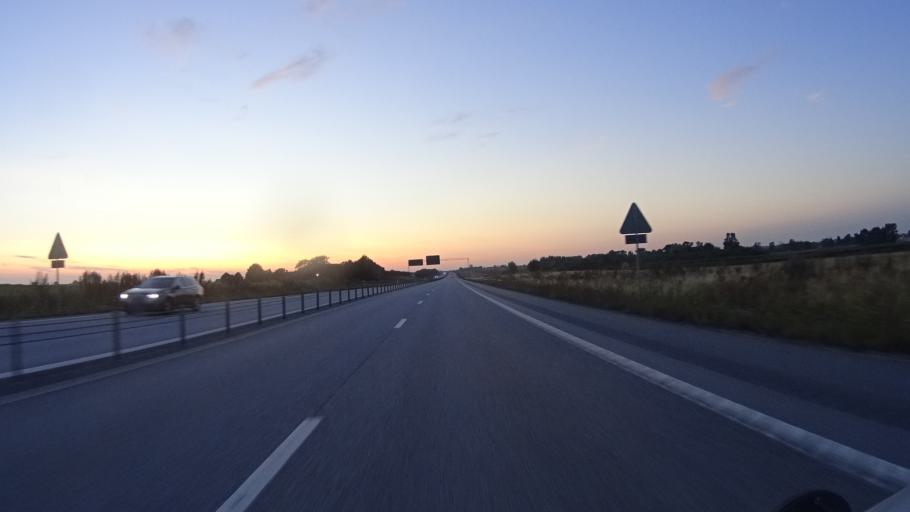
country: SE
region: Skane
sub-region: Trelleborgs Kommun
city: Skare
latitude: 55.3907
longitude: 13.0755
